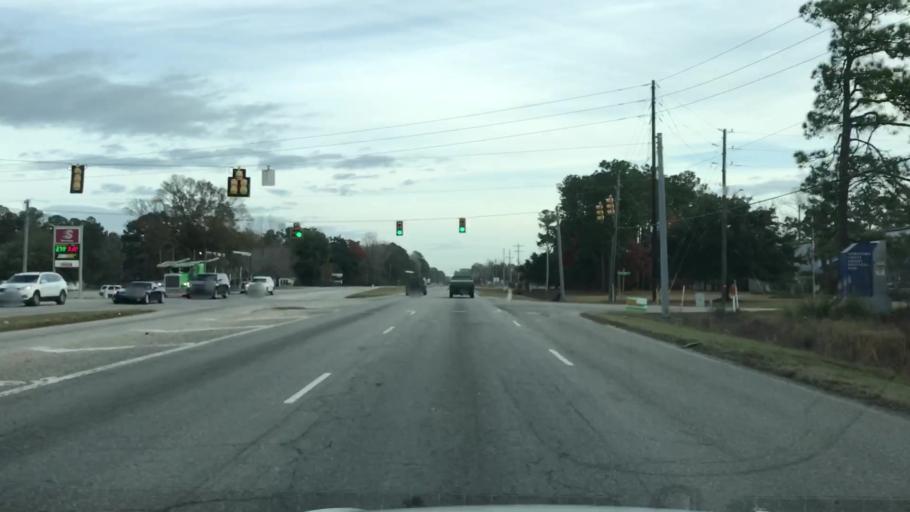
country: US
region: South Carolina
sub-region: Georgetown County
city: Georgetown
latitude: 33.3263
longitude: -79.3165
